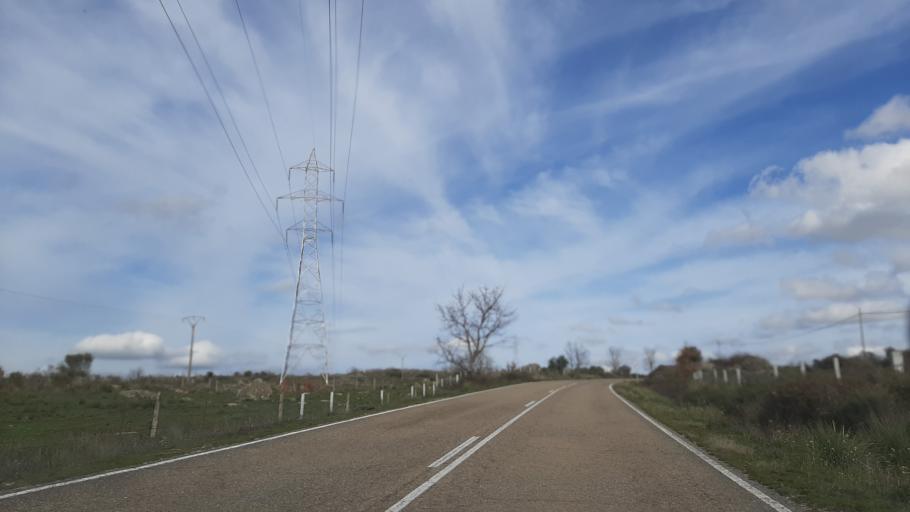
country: ES
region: Castille and Leon
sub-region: Provincia de Salamanca
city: Villarino de los Aires
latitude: 41.2428
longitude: -6.5094
